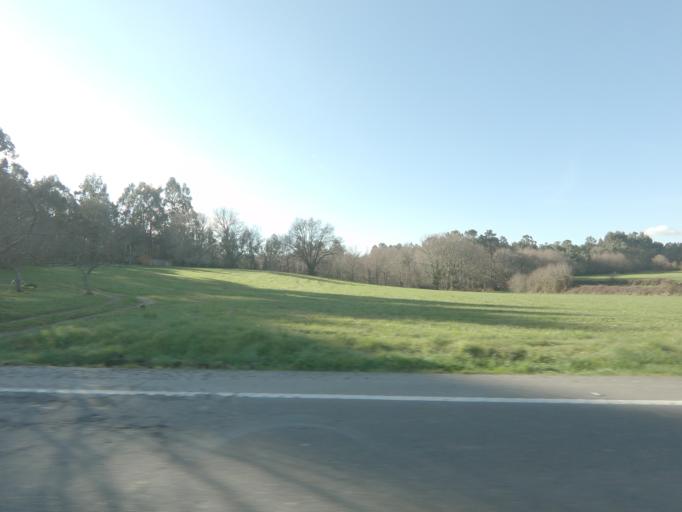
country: ES
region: Galicia
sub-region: Provincia de Pontevedra
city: Silleda
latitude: 42.7127
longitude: -8.2934
